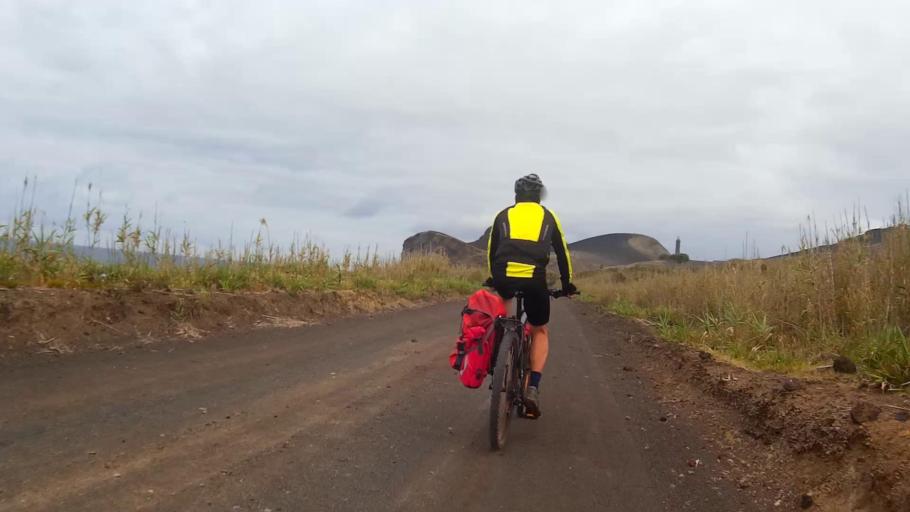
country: PT
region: Azores
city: Ribeira Grande
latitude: 38.5905
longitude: -28.8235
